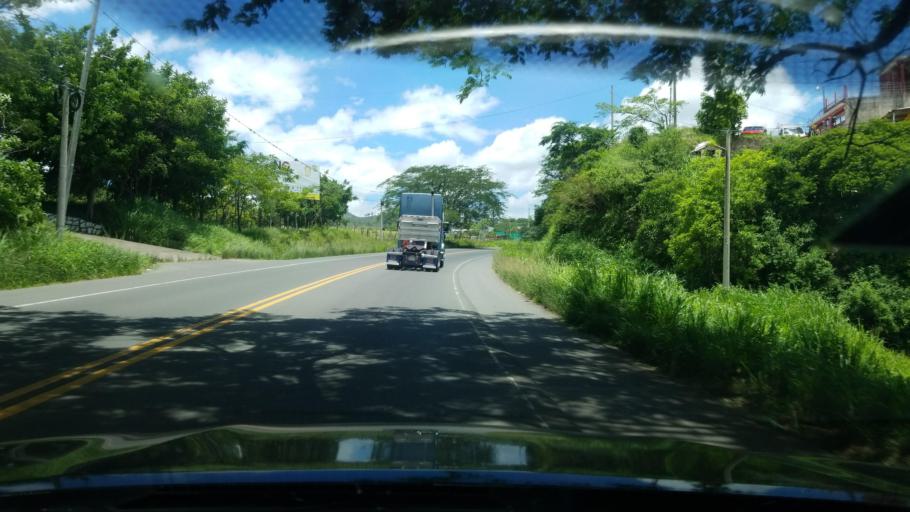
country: HN
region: Francisco Morazan
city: Rio Abajo
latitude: 14.1512
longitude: -87.2062
